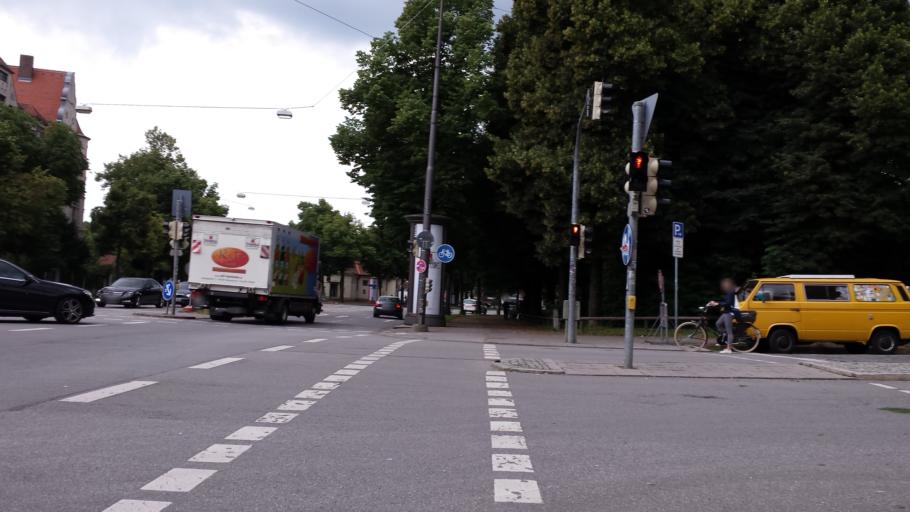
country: DE
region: Bavaria
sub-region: Upper Bavaria
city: Munich
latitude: 48.1377
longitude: 11.5496
